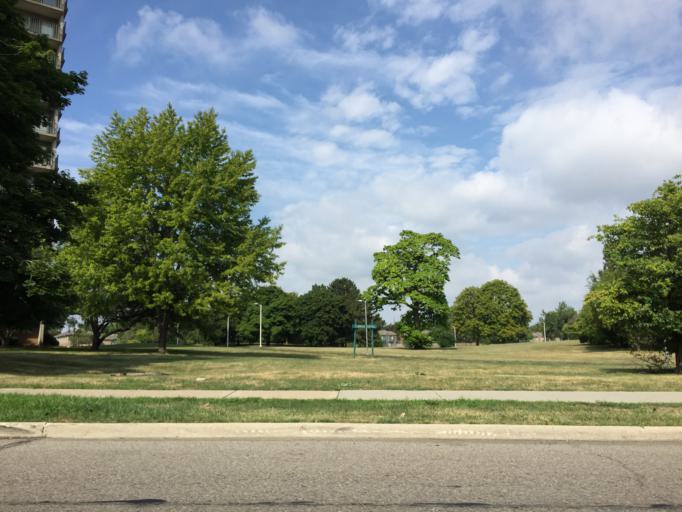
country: US
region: Michigan
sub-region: Wayne County
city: Detroit
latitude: 42.3442
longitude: -83.0266
